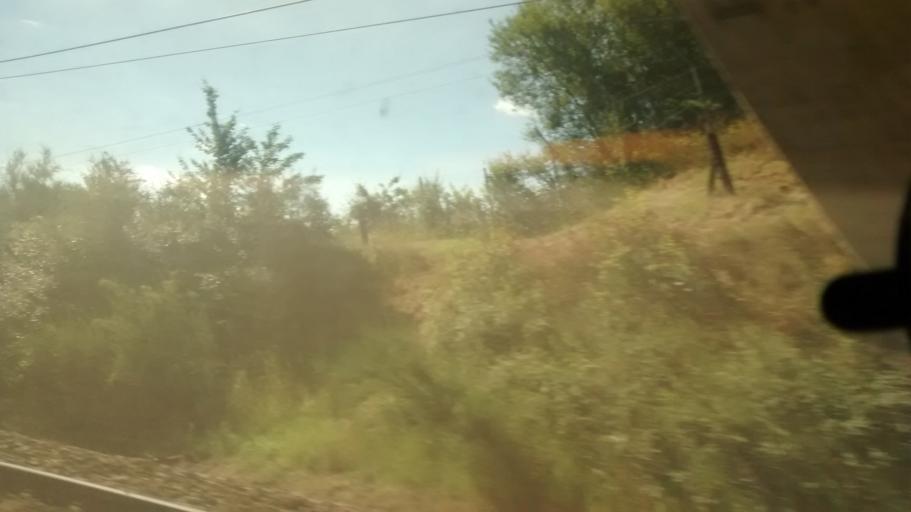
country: FR
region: Pays de la Loire
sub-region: Departement de la Sarthe
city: Thorigne-sur-Due
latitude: 48.0462
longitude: 0.5482
